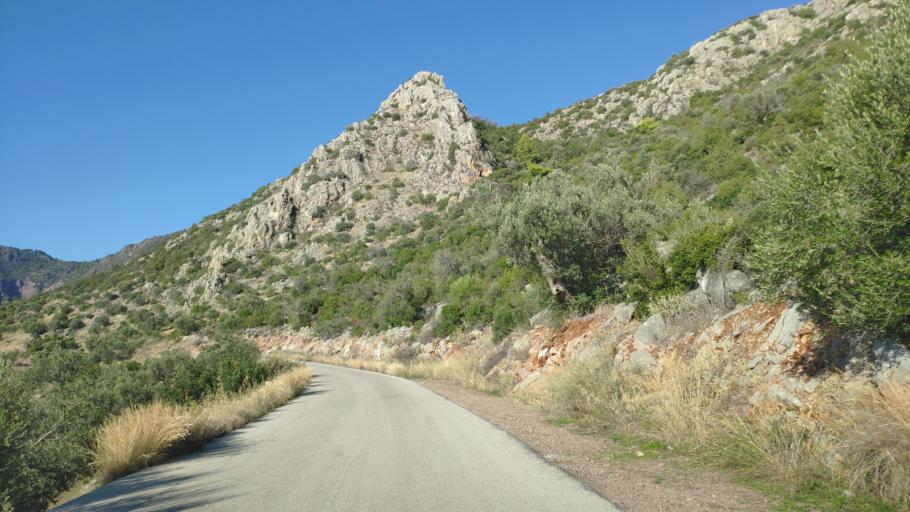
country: GR
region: Attica
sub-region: Nomos Piraios
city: Galatas
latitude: 37.5749
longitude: 23.3601
